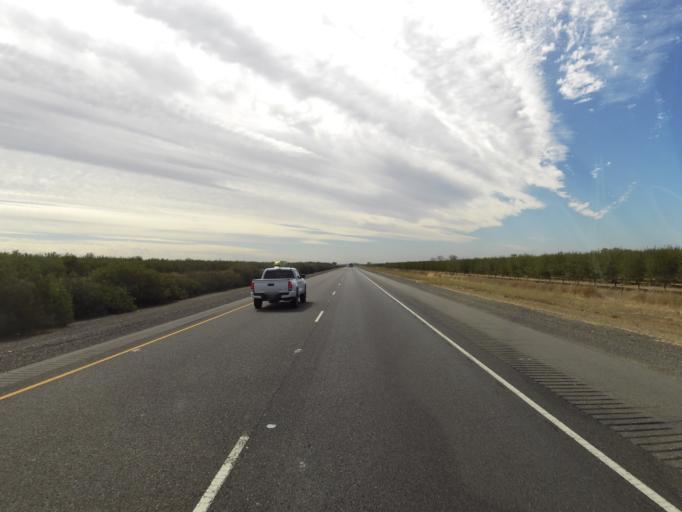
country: US
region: California
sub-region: Glenn County
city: Orland
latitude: 39.6532
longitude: -122.2045
